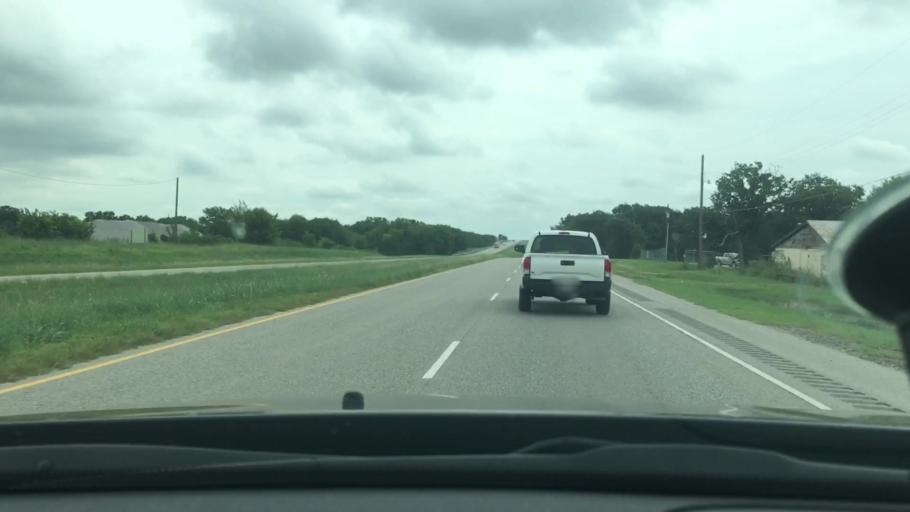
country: US
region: Oklahoma
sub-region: Carter County
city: Wilson
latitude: 34.1729
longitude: -97.4559
